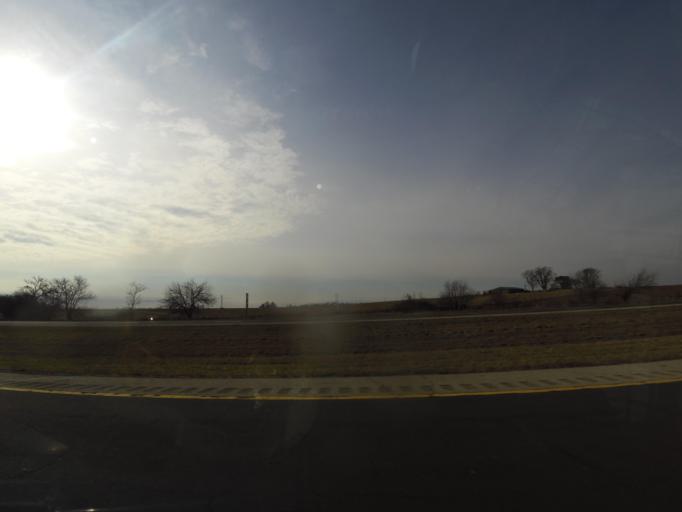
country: US
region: Illinois
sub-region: Macon County
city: Decatur
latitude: 39.7926
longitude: -88.9964
